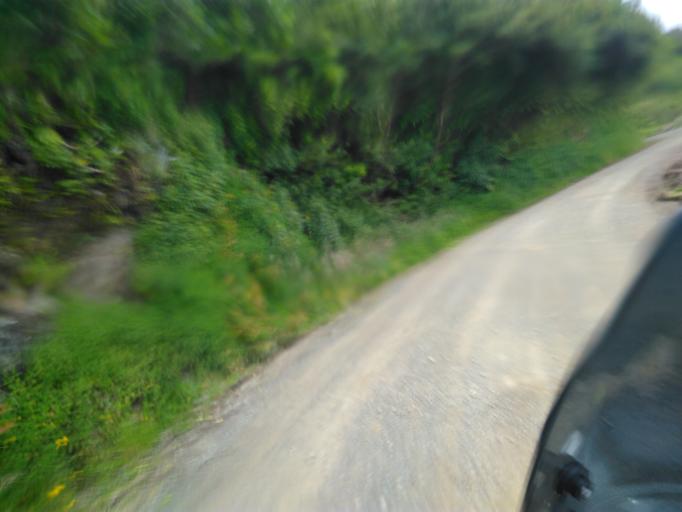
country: NZ
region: Bay of Plenty
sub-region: Opotiki District
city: Opotiki
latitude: -38.0929
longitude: 177.4855
